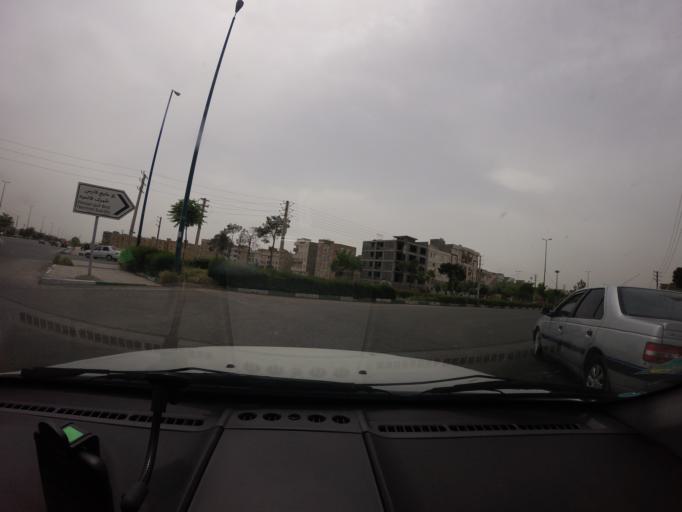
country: IR
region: Tehran
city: Eslamshahr
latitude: 35.5386
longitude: 51.2225
